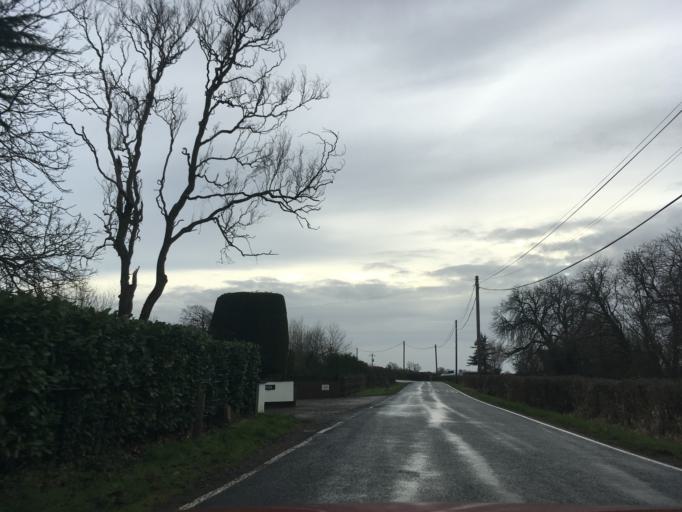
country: GB
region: Wales
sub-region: Newport
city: Goldcliff
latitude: 51.5604
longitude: -2.9097
